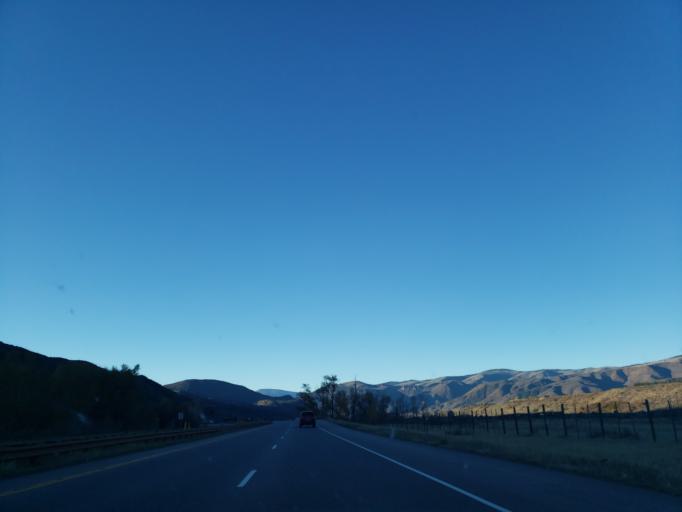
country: US
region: Colorado
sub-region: Pitkin County
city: Aspen
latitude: 39.2327
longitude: -106.8707
